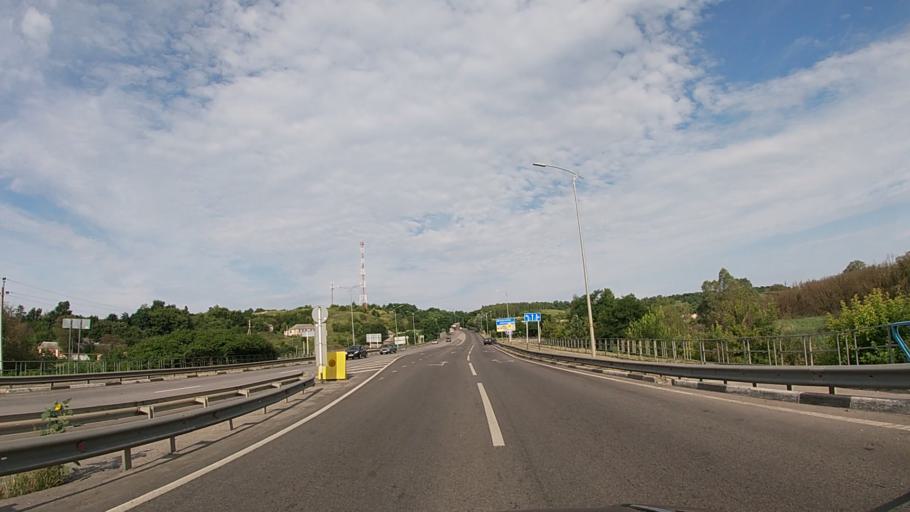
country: RU
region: Belgorod
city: Severnyy
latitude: 50.6357
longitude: 36.4631
